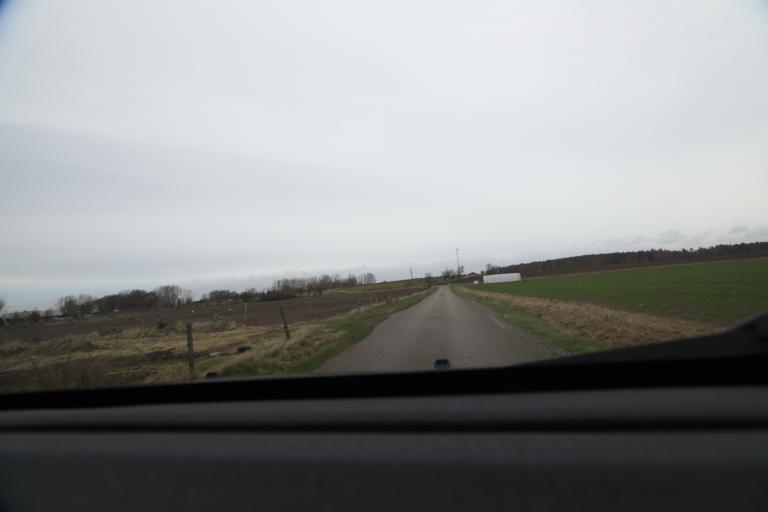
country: SE
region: Halland
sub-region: Varbergs Kommun
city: Traslovslage
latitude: 57.0755
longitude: 12.3021
